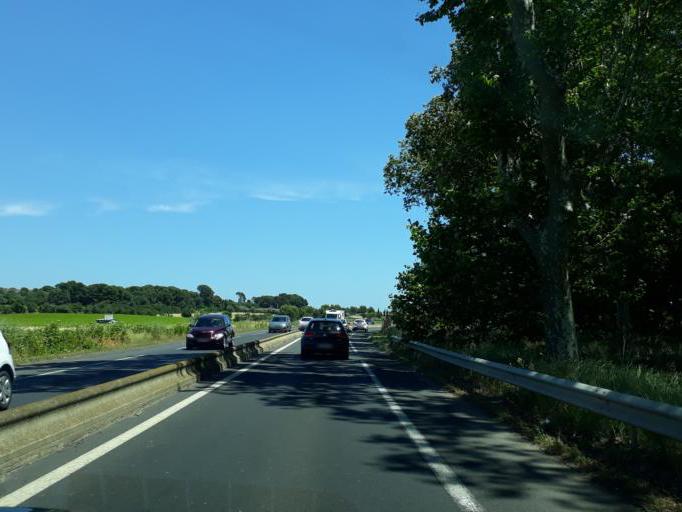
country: FR
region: Languedoc-Roussillon
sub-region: Departement de l'Herault
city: Cers
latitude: 43.3164
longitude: 3.3091
